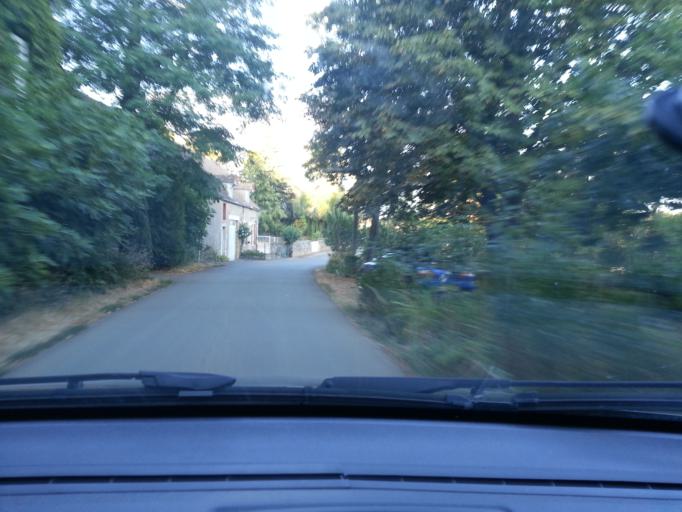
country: FR
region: Bourgogne
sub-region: Departement de Saone-et-Loire
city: Givry
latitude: 46.7590
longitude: 4.7081
